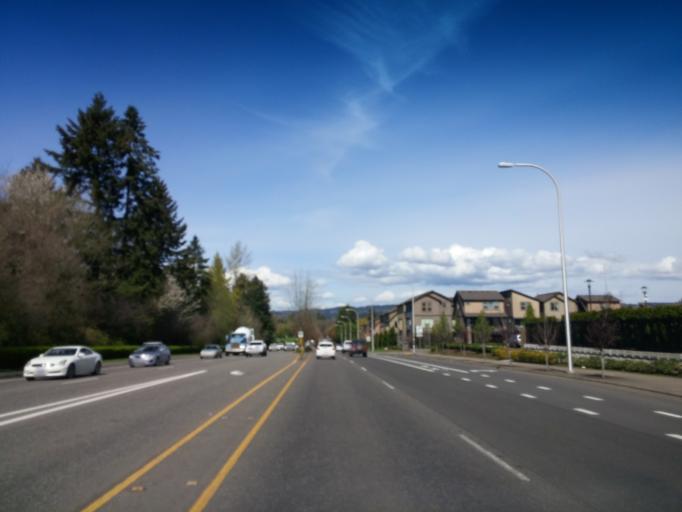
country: US
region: Oregon
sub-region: Washington County
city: Cedar Mill
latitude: 45.5043
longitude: -122.8263
